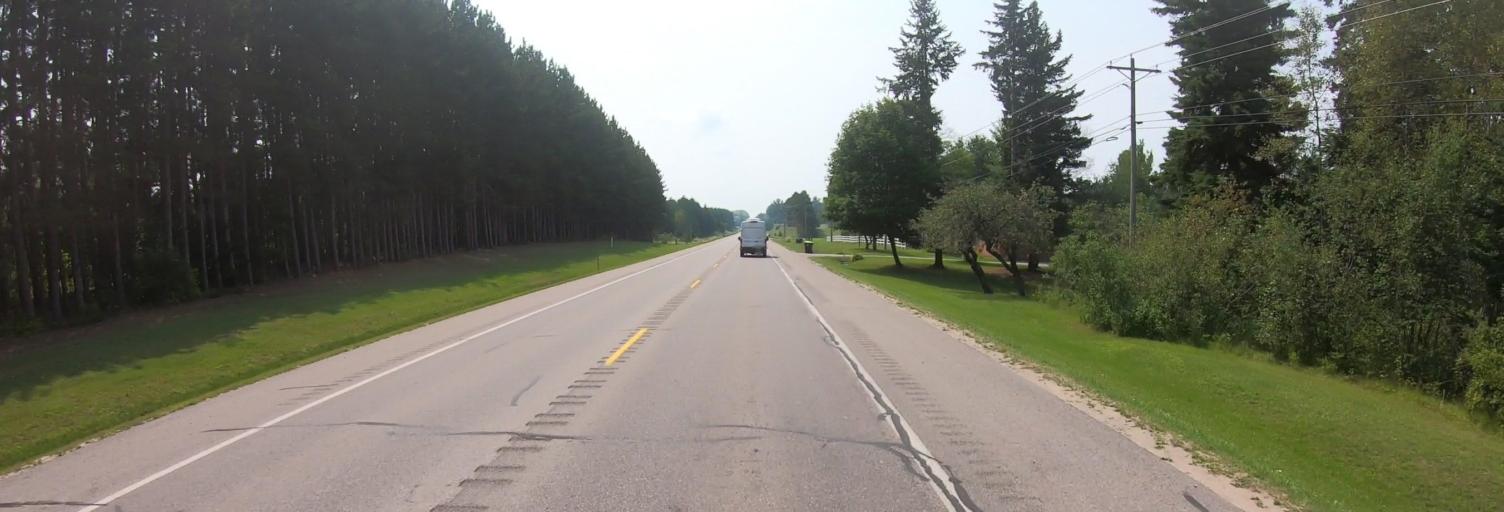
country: US
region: Michigan
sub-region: Luce County
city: Newberry
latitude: 46.3124
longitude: -85.5097
